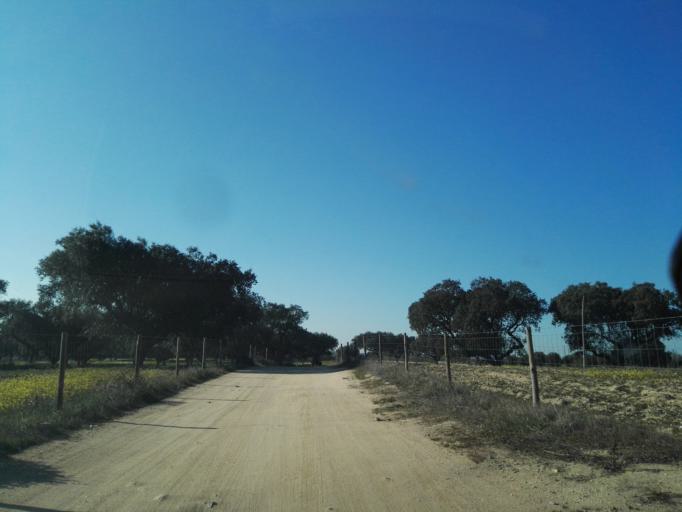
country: PT
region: Evora
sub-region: Evora
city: Evora
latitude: 38.5434
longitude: -7.9471
